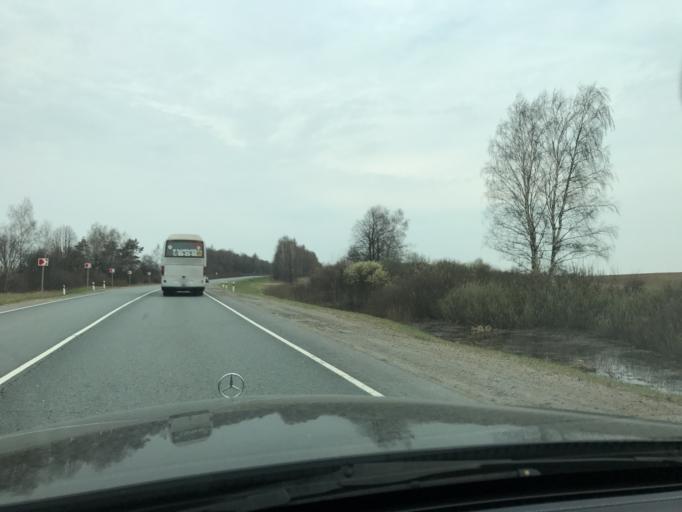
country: RU
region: Vladimir
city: Suzdal'
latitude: 56.3590
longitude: 40.4680
